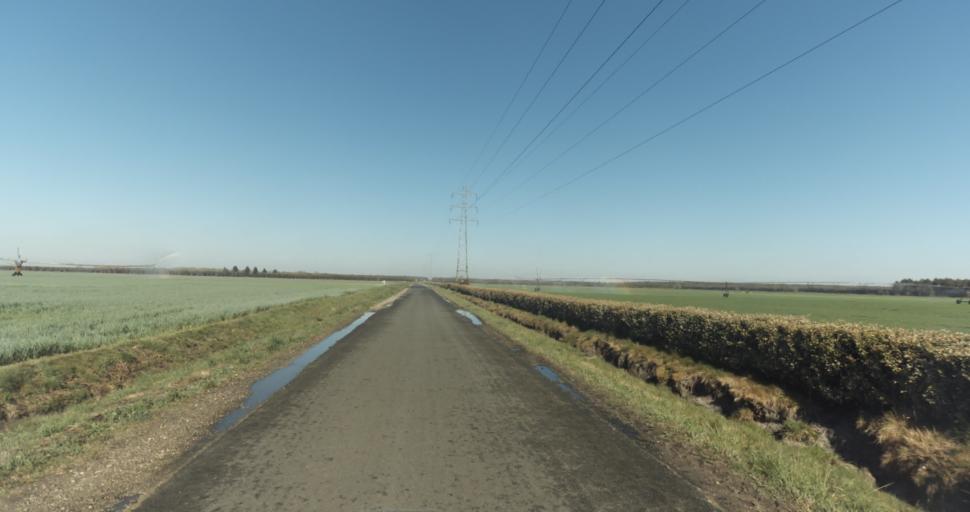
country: FR
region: Aquitaine
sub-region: Departement de la Gironde
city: Marcheprime
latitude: 44.7454
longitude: -0.8343
